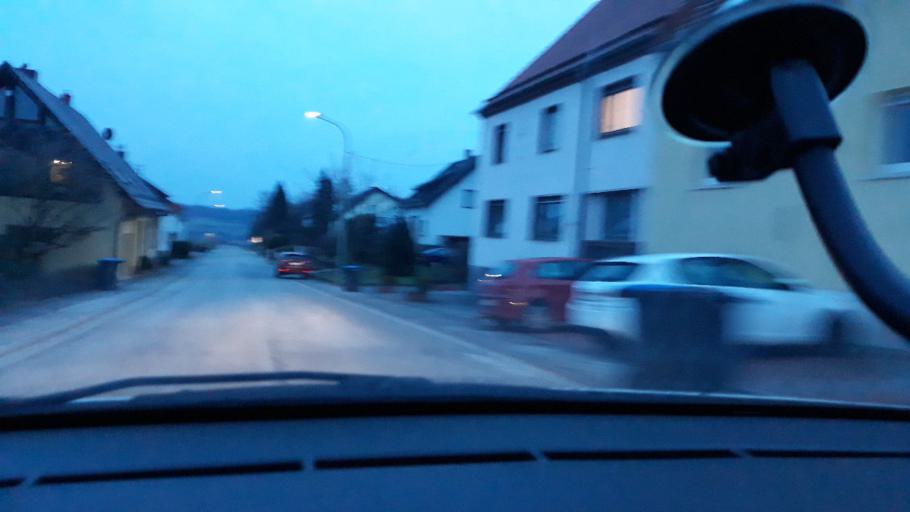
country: DE
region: Saarland
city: Blieskastel
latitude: 49.2177
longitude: 7.2033
